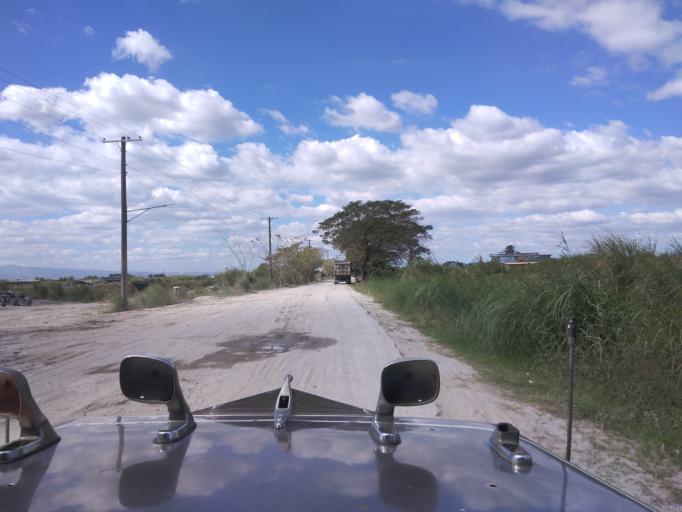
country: PH
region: Central Luzon
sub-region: Province of Pampanga
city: Magliman
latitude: 15.0391
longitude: 120.6312
